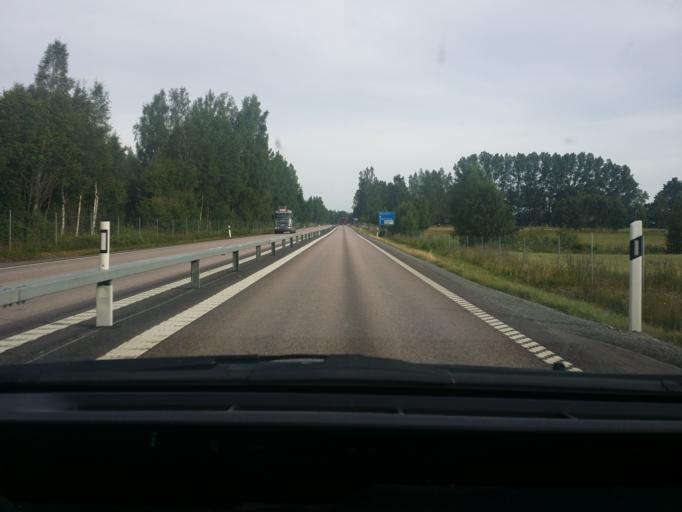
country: SE
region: Vaestmanland
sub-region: Sala Kommun
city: Sala
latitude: 59.8238
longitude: 16.5361
